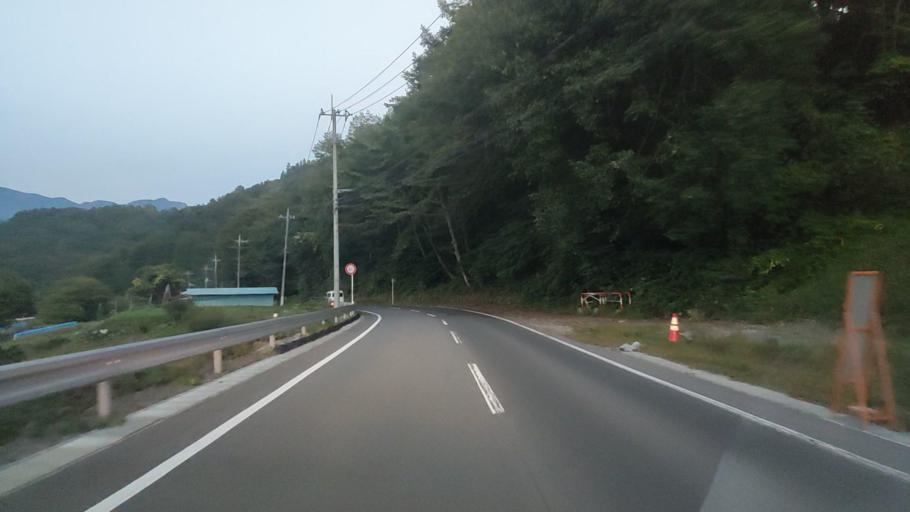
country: JP
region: Gunma
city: Nakanojomachi
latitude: 36.5456
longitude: 138.6017
